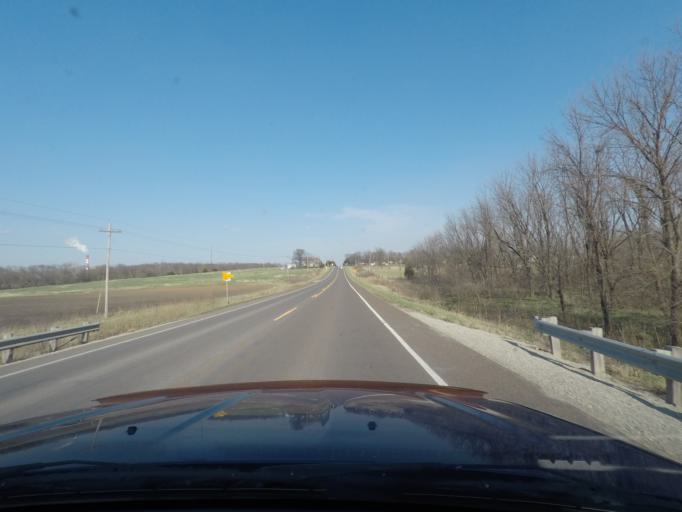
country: US
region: Kansas
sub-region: Douglas County
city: Lawrence
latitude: 39.0006
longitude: -95.2834
